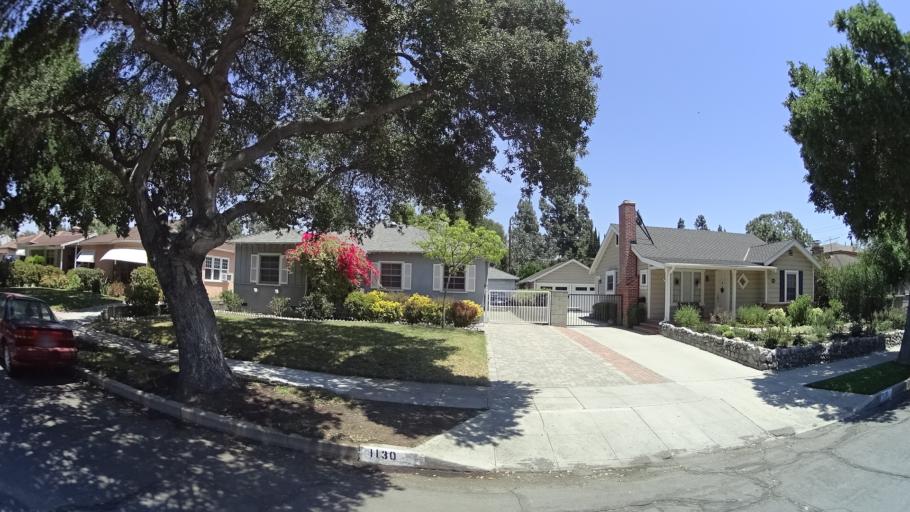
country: US
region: California
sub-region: Los Angeles County
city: Burbank
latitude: 34.1744
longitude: -118.3431
